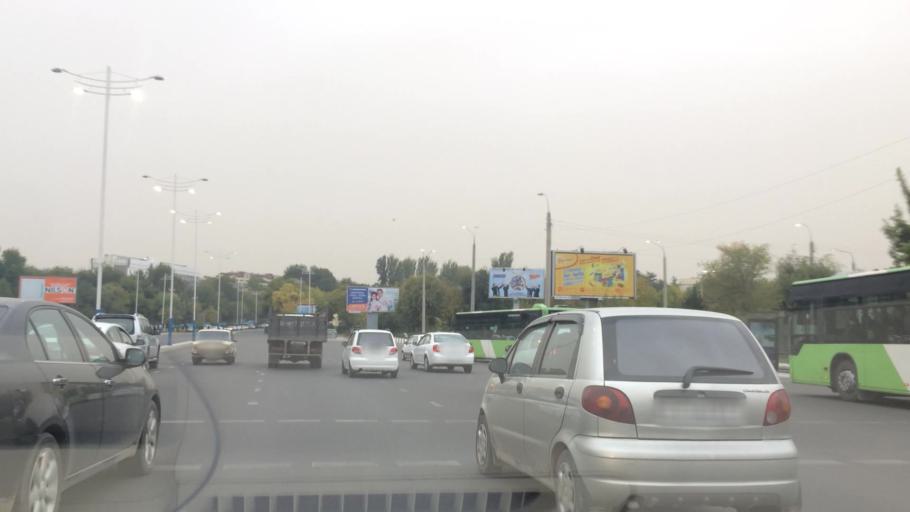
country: UZ
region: Toshkent Shahri
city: Tashkent
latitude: 41.3077
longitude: 69.2993
